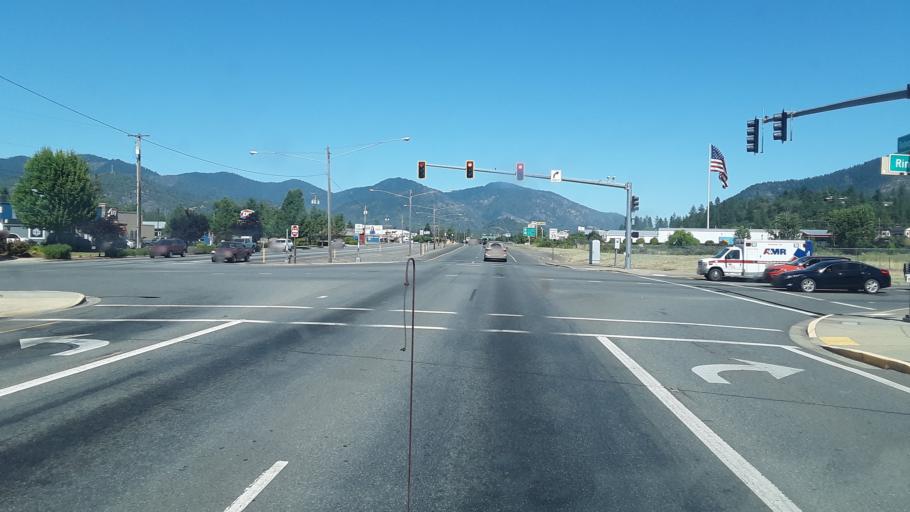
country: US
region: Oregon
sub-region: Josephine County
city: Grants Pass
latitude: 42.4233
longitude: -123.3404
